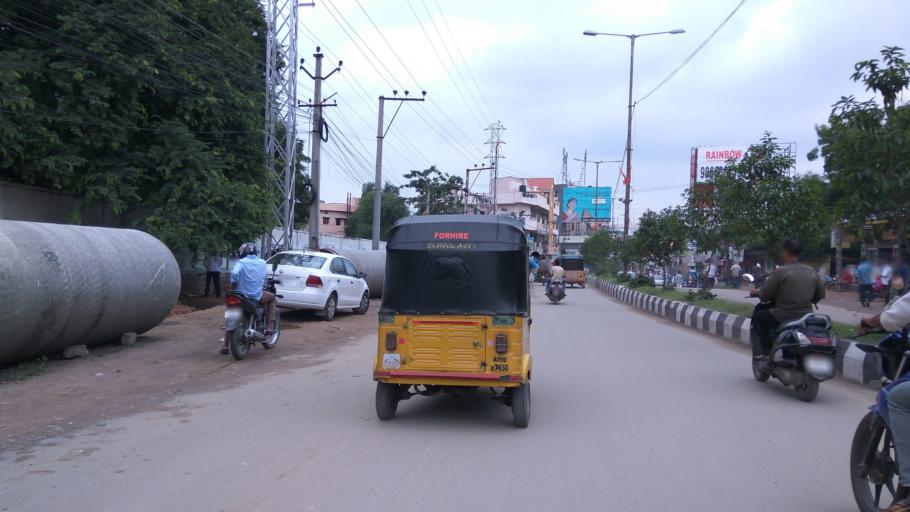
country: IN
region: Telangana
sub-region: Hyderabad
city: Malkajgiri
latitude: 17.4598
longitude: 78.5359
